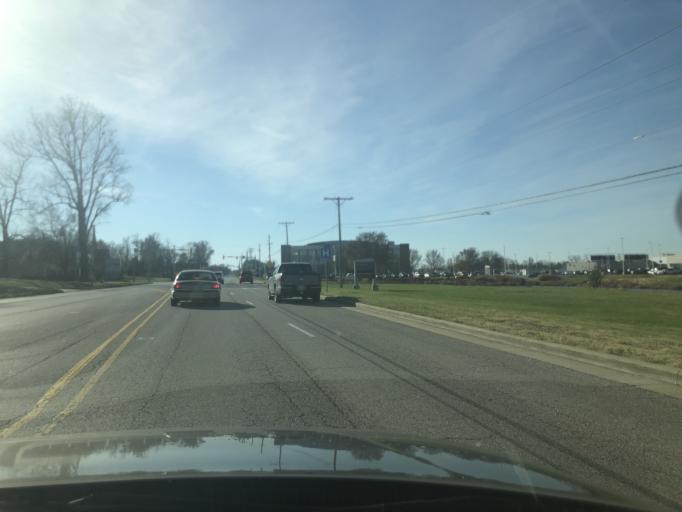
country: US
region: Indiana
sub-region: Warrick County
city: Newburgh
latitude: 37.9758
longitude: -87.4413
